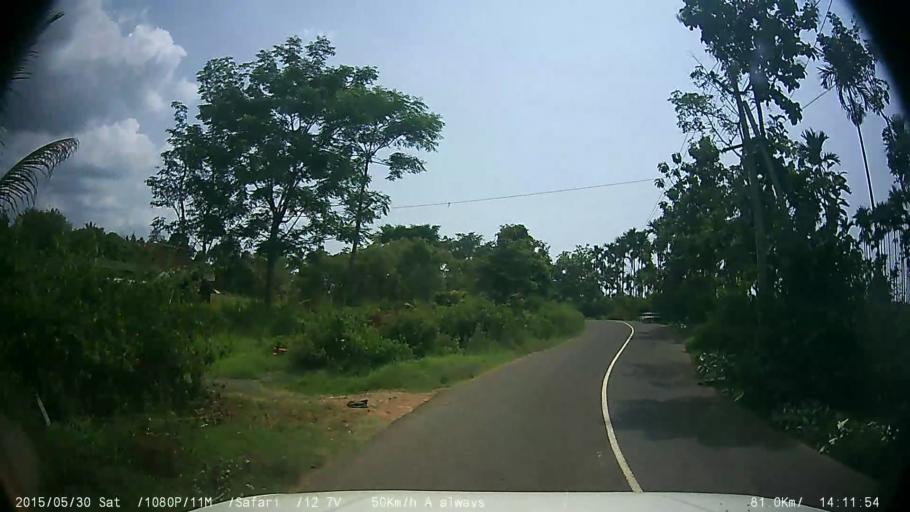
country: IN
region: Kerala
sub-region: Wayanad
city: Panamaram
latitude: 11.7904
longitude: 76.0512
